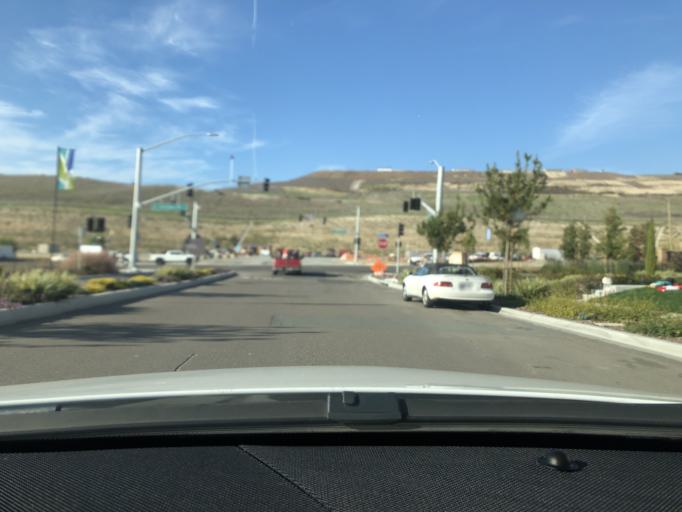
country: US
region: California
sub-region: San Diego County
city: Bonita
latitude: 32.5979
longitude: -117.0039
